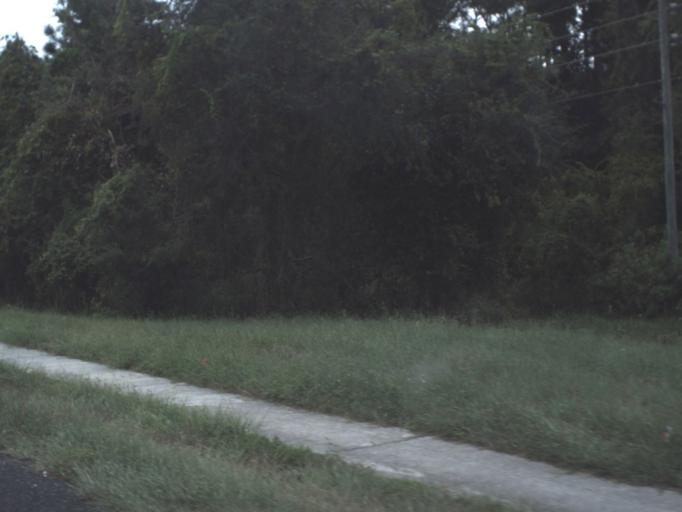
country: US
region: Florida
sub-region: Hernando County
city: Timber Pines
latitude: 28.4713
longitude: -82.6179
